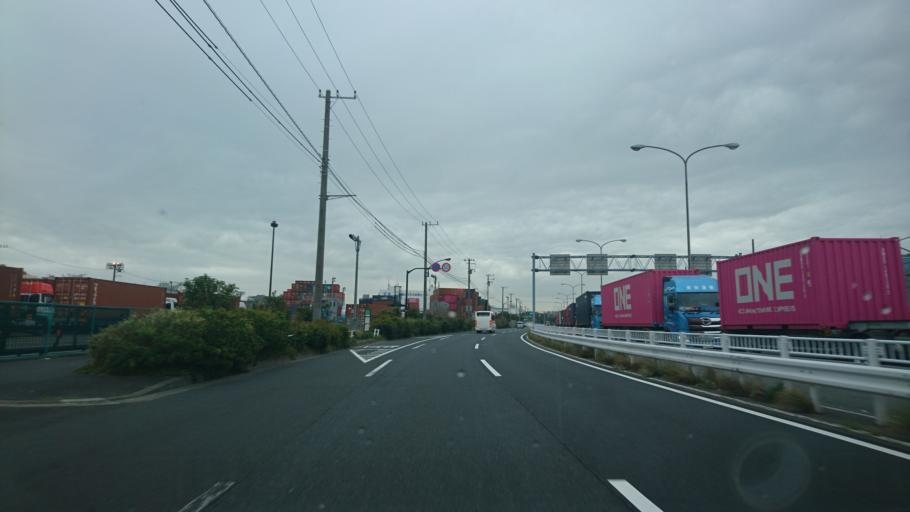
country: JP
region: Kanagawa
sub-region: Kawasaki-shi
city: Kawasaki
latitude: 35.6043
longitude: 139.7608
